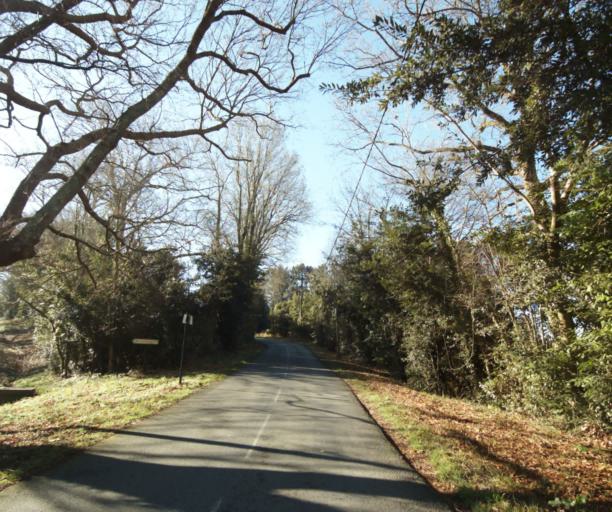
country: FR
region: Aquitaine
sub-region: Departement des Pyrenees-Atlantiques
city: Ciboure
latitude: 43.3632
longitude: -1.6608
